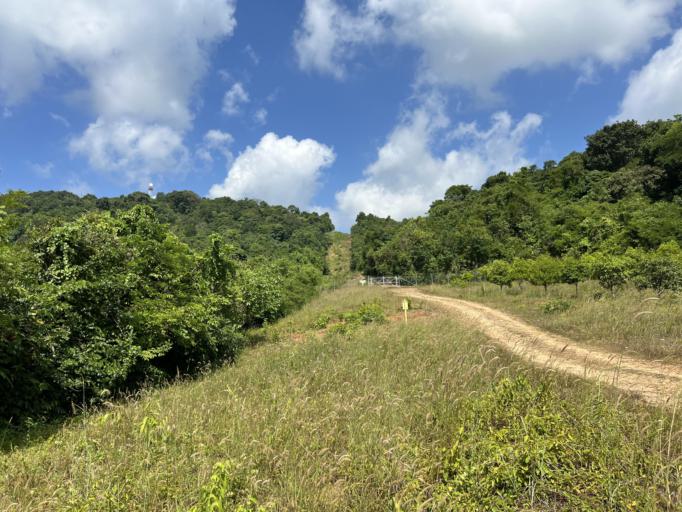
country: MM
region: Tanintharyi
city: Dawei
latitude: 14.6043
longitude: 97.9728
